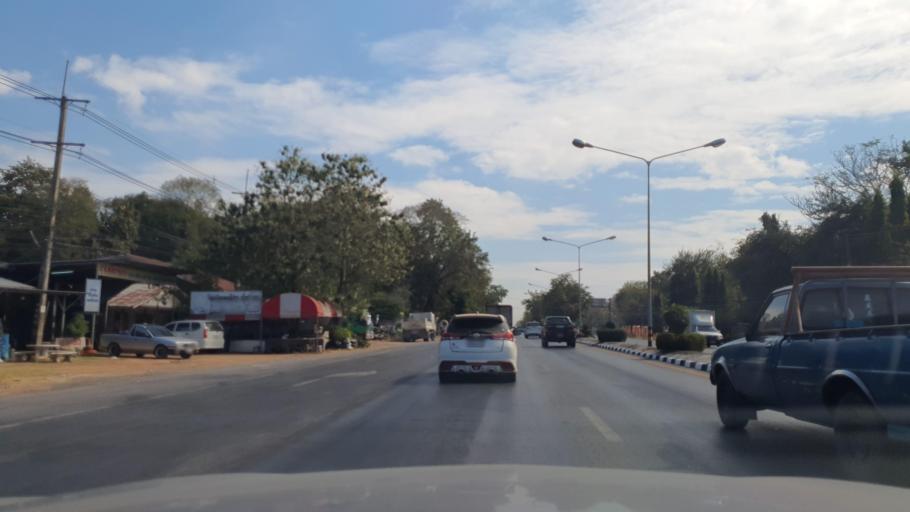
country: TH
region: Kalasin
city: Yang Talat
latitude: 16.4062
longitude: 103.4160
